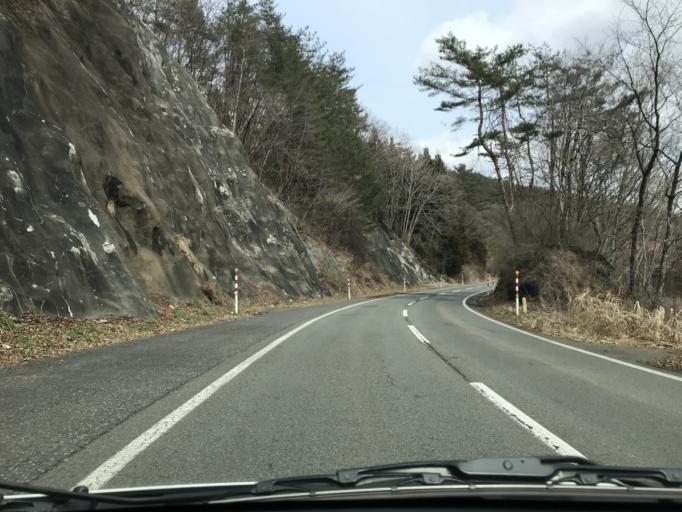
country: JP
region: Iwate
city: Tono
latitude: 39.3009
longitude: 141.3657
